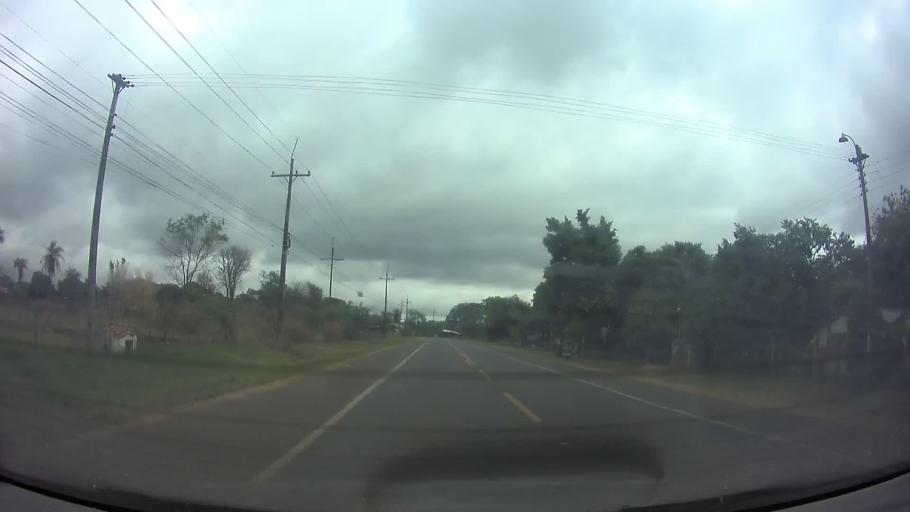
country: PY
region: Central
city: Guarambare
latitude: -25.5013
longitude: -57.4936
